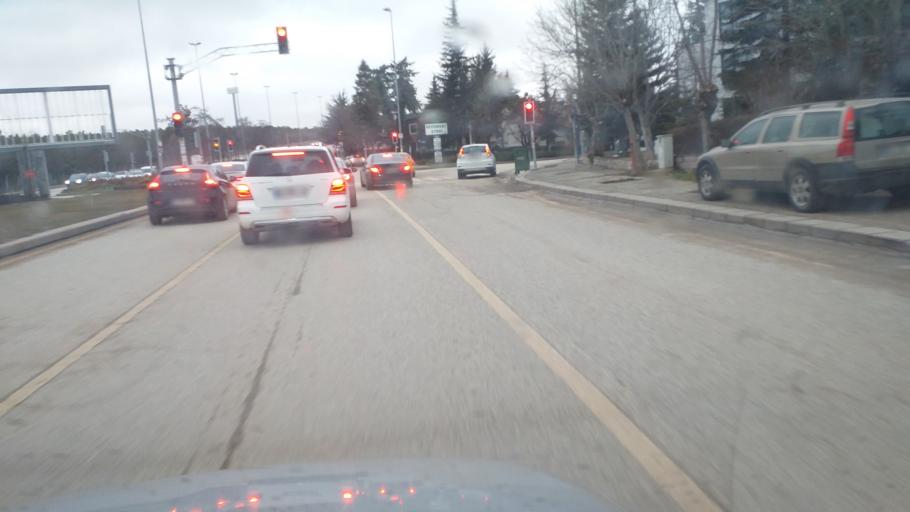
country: TR
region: Ankara
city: Batikent
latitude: 39.8944
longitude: 32.7291
